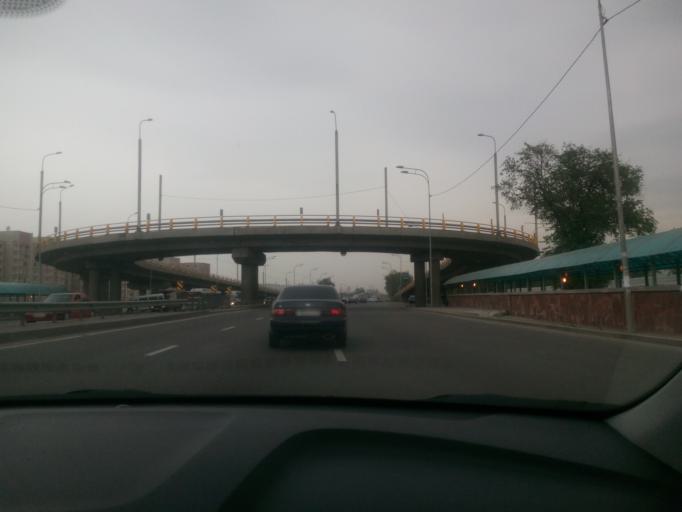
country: KZ
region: Almaty Qalasy
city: Almaty
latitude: 43.2399
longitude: 76.8136
